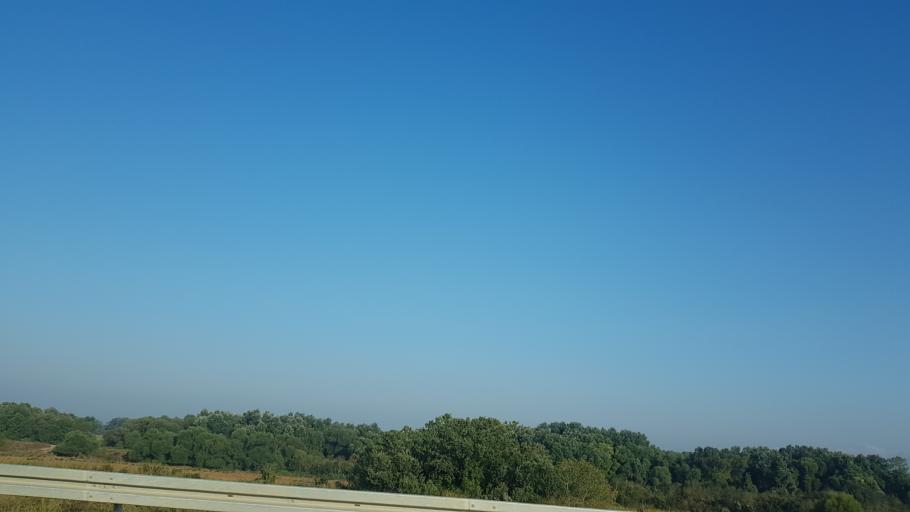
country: TR
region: Bursa
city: Karacabey
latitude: 40.1670
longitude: 28.3199
